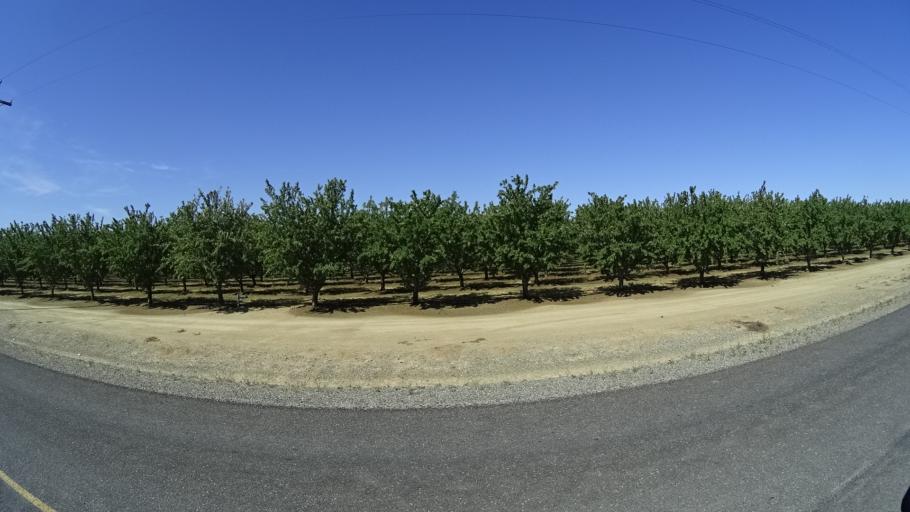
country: US
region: California
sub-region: Glenn County
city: Hamilton City
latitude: 39.6929
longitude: -122.1032
